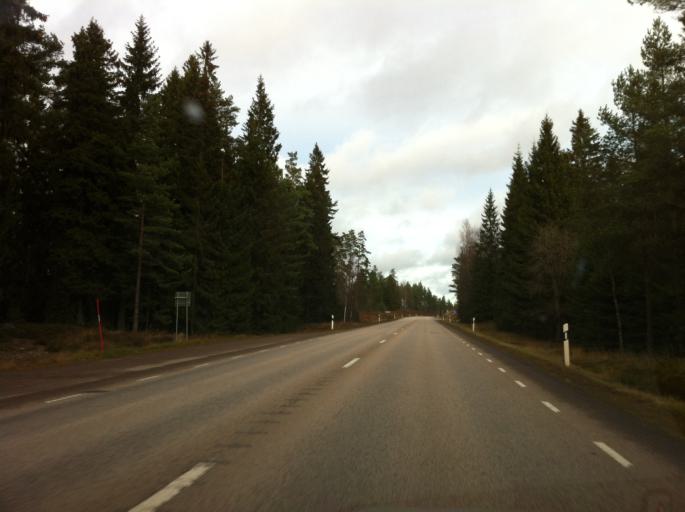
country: SE
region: Kronoberg
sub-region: Uppvidinge Kommun
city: Lenhovda
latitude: 57.1156
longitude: 15.2184
